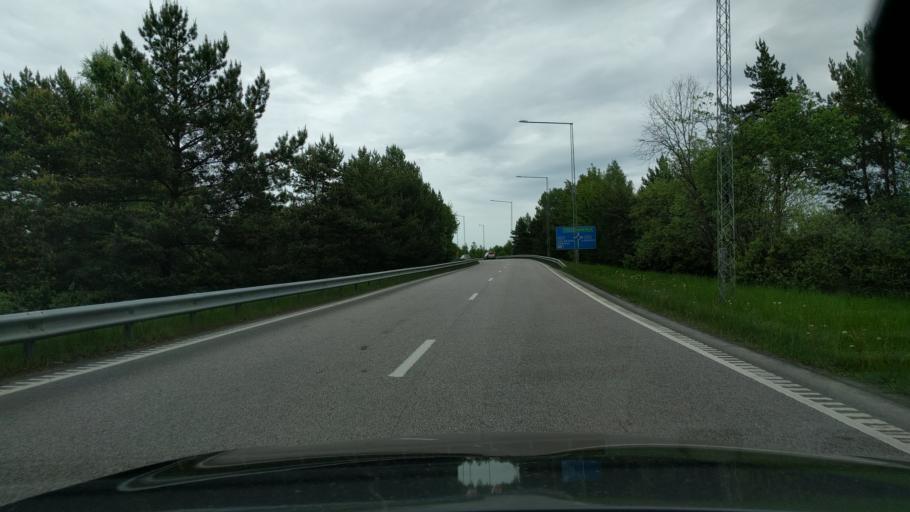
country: SE
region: Stockholm
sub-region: Taby Kommun
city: Taby
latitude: 59.4542
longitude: 18.1348
